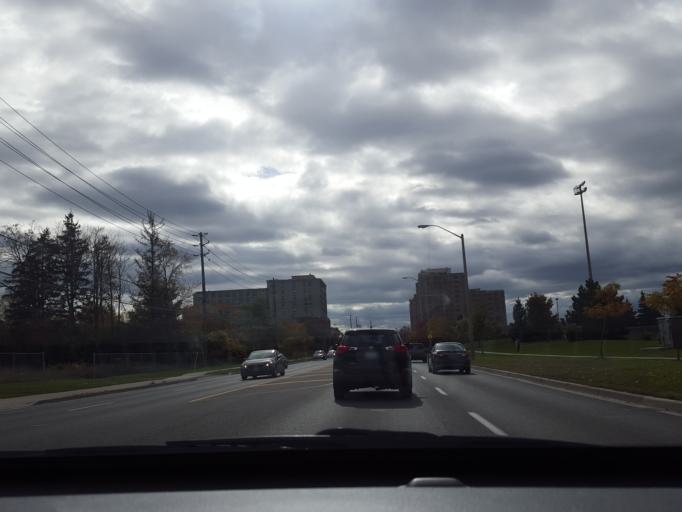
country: CA
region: Ontario
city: Markham
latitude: 43.8154
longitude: -79.3035
